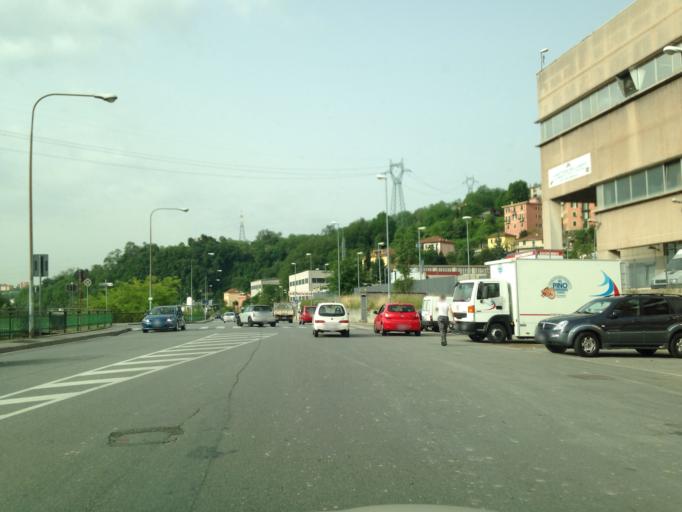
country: IT
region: Liguria
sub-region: Provincia di Genova
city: Santa Marta
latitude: 44.4892
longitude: 8.8993
